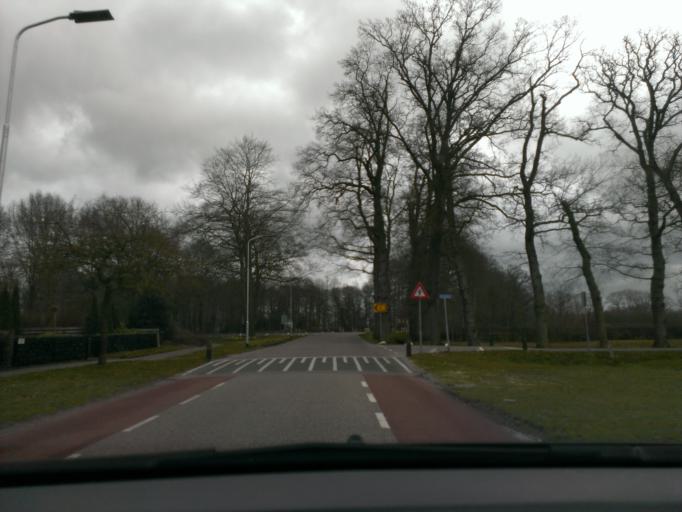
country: NL
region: Gelderland
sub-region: Gemeente Heerde
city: Heerde
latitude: 52.3807
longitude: 6.0410
